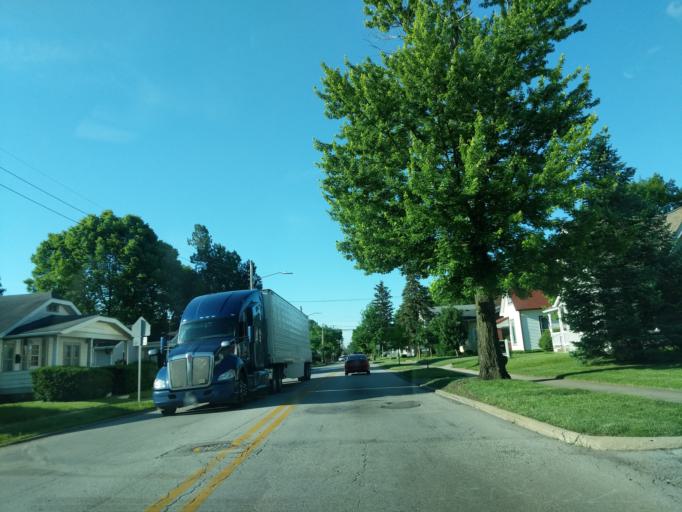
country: US
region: Indiana
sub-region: Hancock County
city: Greenfield
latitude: 39.7931
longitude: -85.7697
